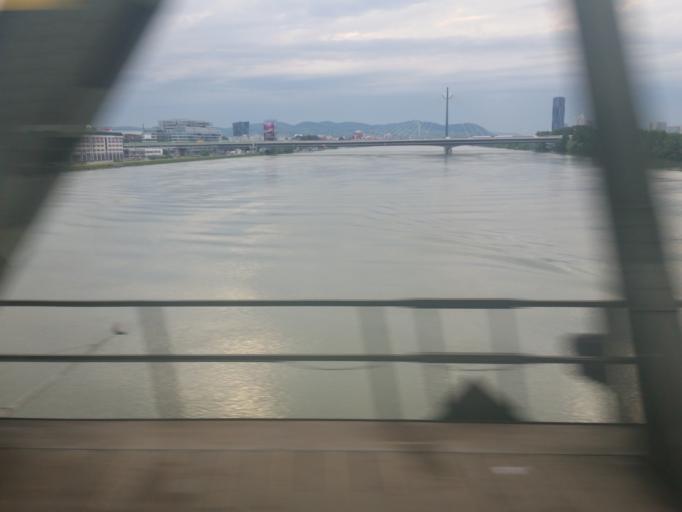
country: AT
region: Lower Austria
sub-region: Politischer Bezirk Wien-Umgebung
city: Schwechat
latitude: 48.2013
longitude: 16.4436
